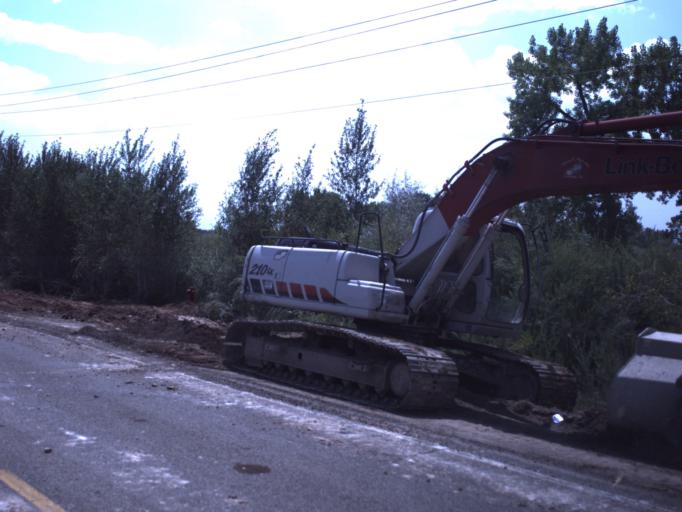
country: US
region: Utah
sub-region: Duchesne County
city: Roosevelt
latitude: 40.3911
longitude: -110.0298
